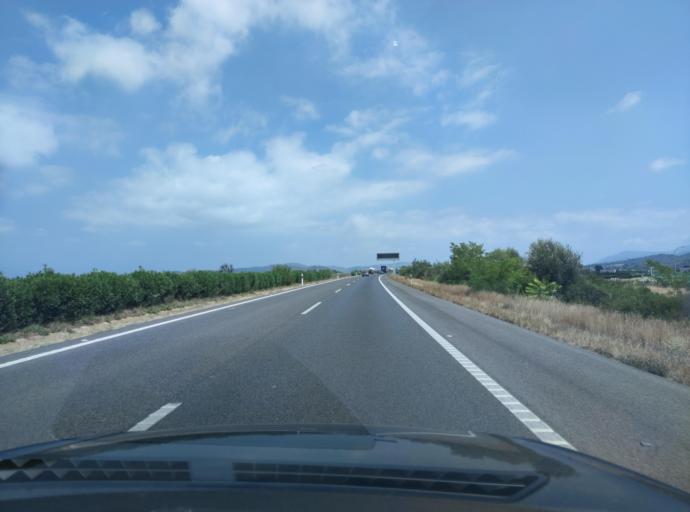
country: ES
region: Catalonia
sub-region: Provincia de Tarragona
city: Ulldecona
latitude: 40.5458
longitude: 0.4197
